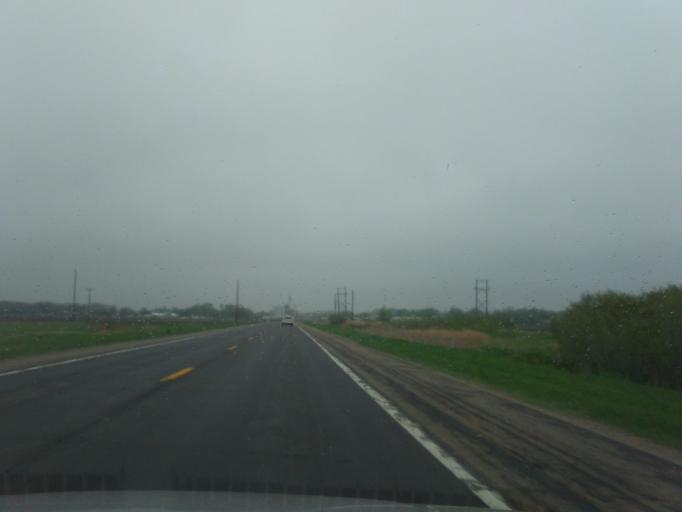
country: US
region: Nebraska
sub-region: Cuming County
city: West Point
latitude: 41.9217
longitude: -96.8002
